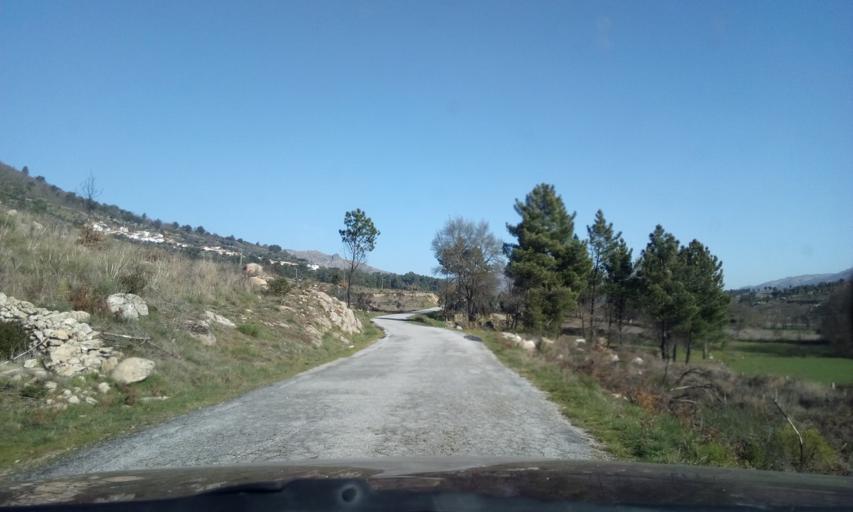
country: PT
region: Guarda
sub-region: Celorico da Beira
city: Celorico da Beira
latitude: 40.6835
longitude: -7.4552
